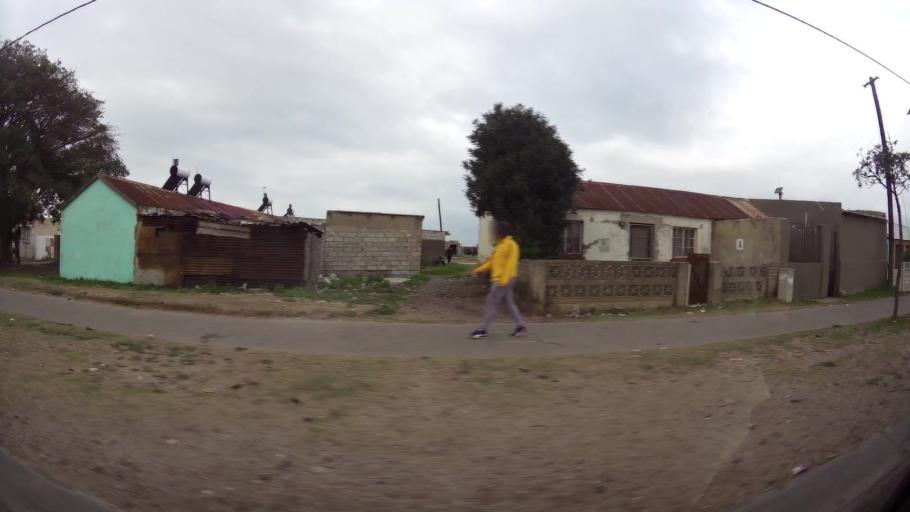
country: ZA
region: Eastern Cape
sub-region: Nelson Mandela Bay Metropolitan Municipality
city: Port Elizabeth
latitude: -33.9027
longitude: 25.5990
